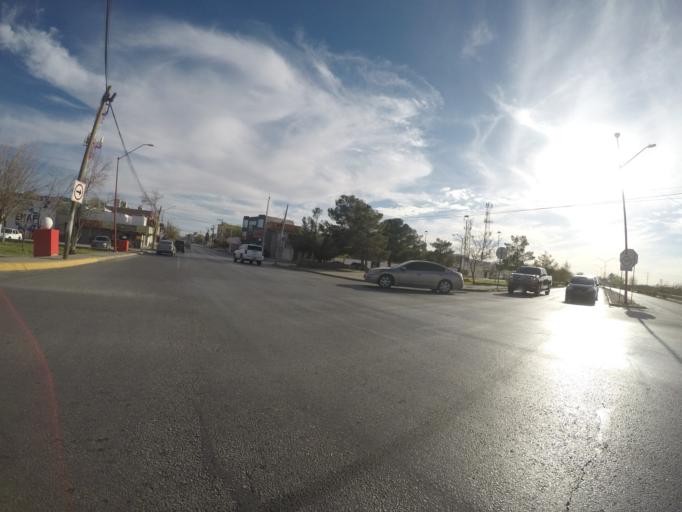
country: US
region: Texas
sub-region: El Paso County
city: El Paso
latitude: 31.7544
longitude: -106.4480
